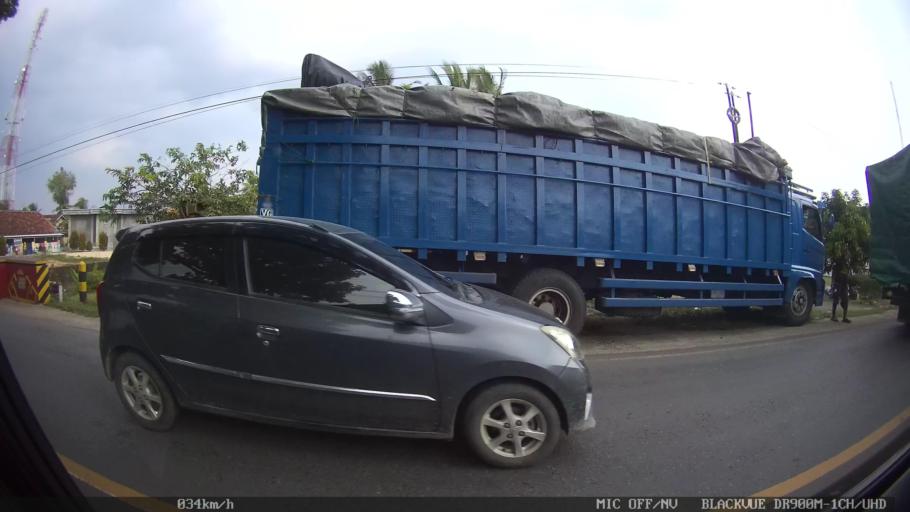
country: ID
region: Lampung
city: Gadingrejo
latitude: -5.3722
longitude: 105.0462
